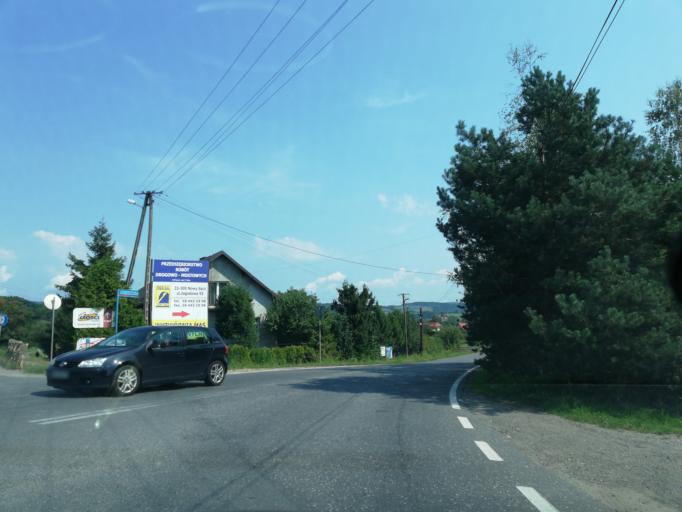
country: PL
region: Lesser Poland Voivodeship
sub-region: Powiat nowosadecki
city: Chelmiec
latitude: 49.6446
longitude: 20.6678
